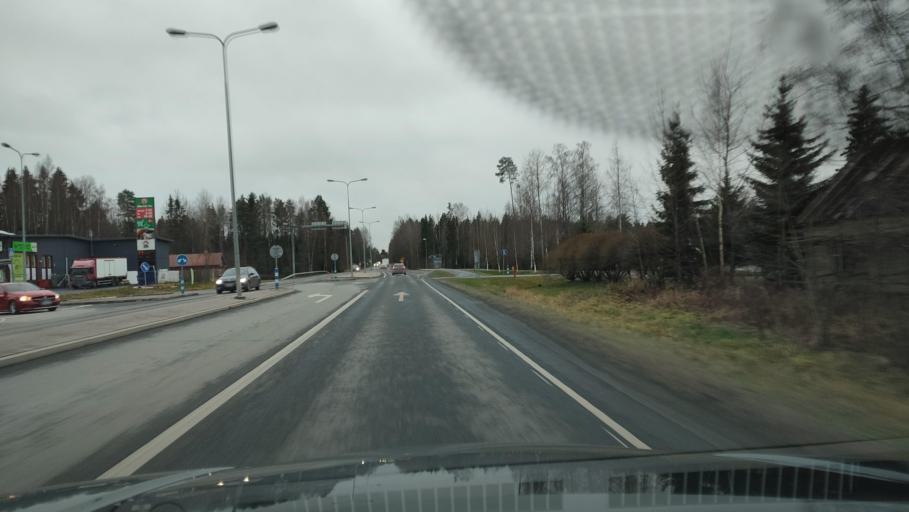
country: FI
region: Southern Ostrobothnia
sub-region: Seinaejoki
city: Ilmajoki
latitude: 62.7707
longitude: 22.6810
